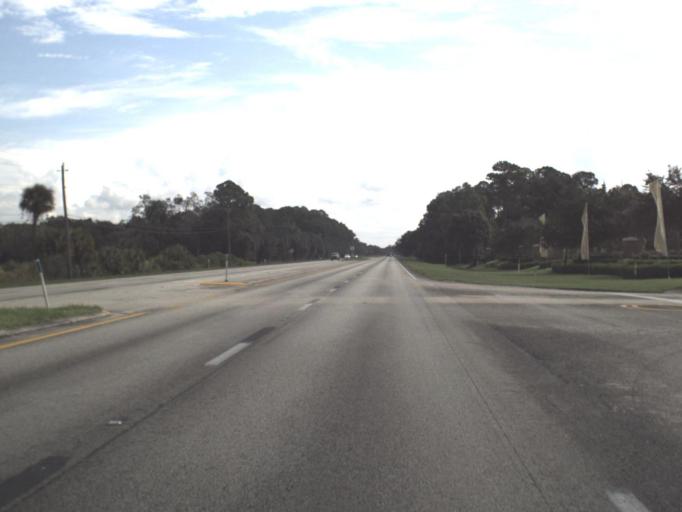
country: US
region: Florida
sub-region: Lee County
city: Olga
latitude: 26.7123
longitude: -81.7085
